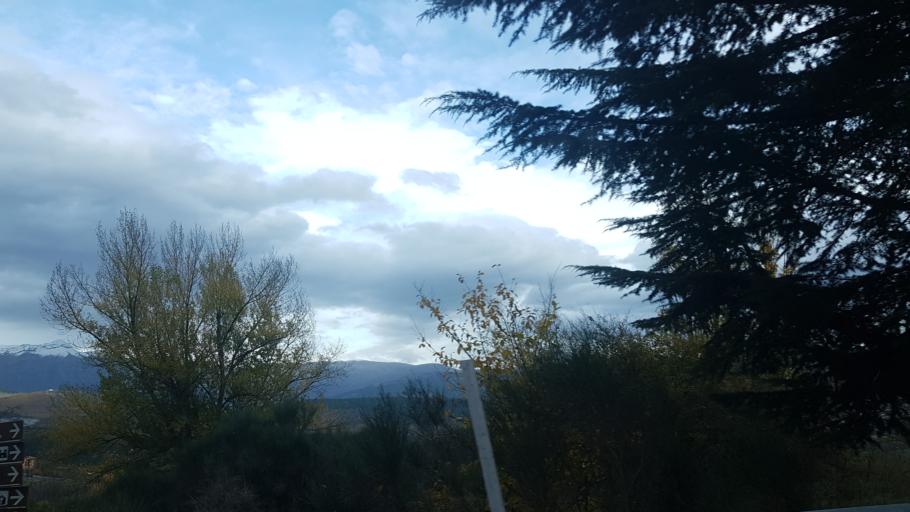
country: IT
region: Abruzzo
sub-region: Provincia dell' Aquila
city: Progetto Case Bazzano
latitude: 42.3608
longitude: 13.4296
